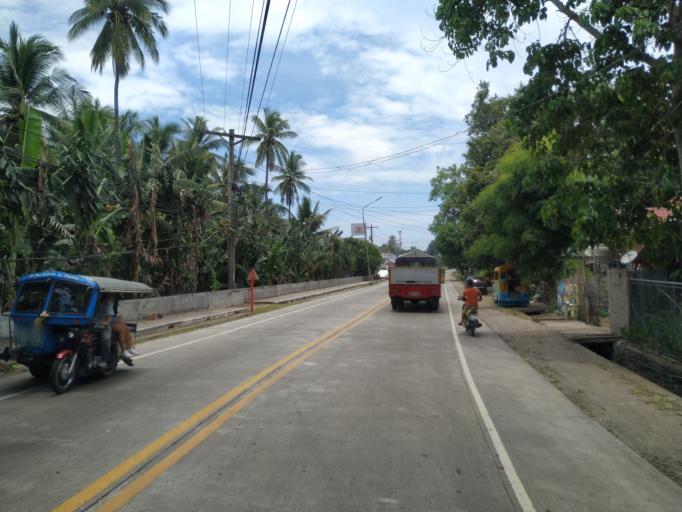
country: PH
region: Central Visayas
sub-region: Province of Negros Oriental
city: Sibulan
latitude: 9.3527
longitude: 123.2845
